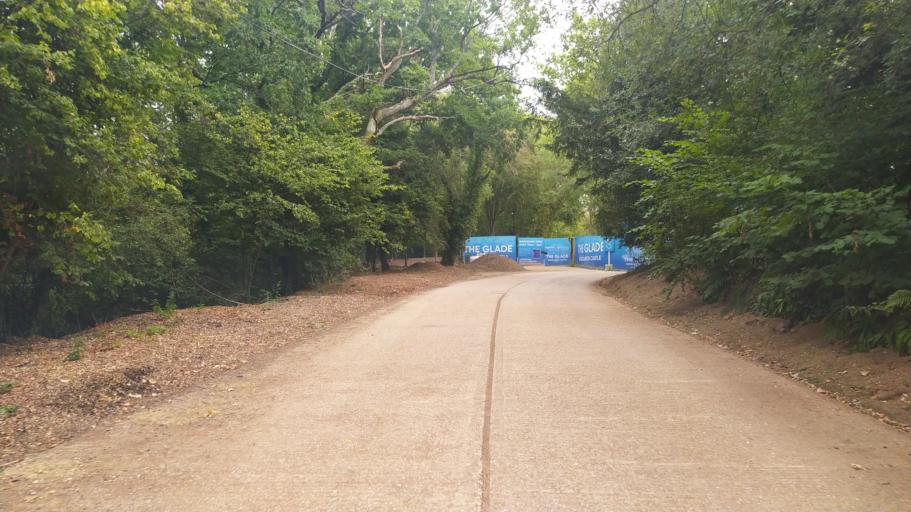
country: GB
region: England
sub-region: Hampshire
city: Havant
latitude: 50.8887
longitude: -0.9610
